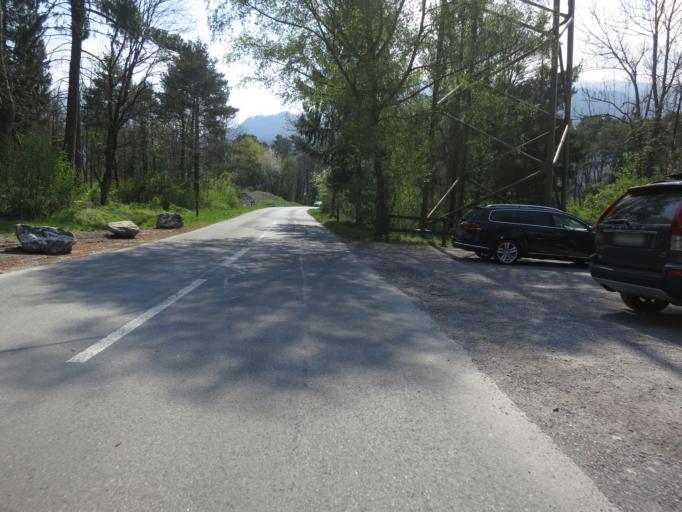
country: CH
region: Saint Gallen
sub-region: Wahlkreis Sarganserland
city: Bad Ragaz
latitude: 47.0227
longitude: 9.4993
